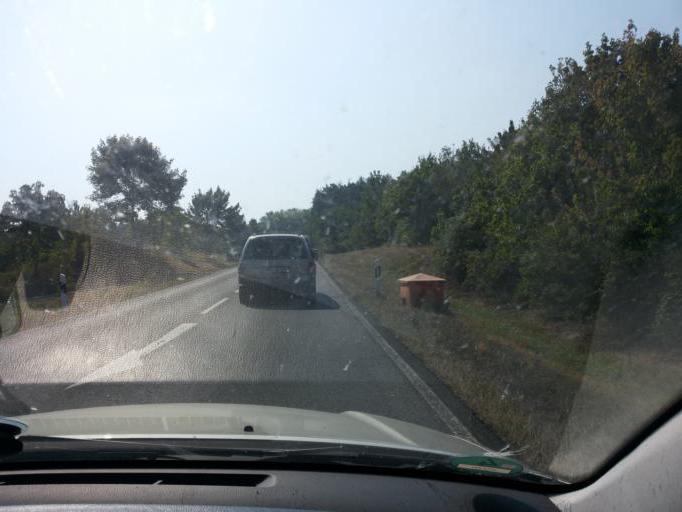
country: DE
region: Bavaria
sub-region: Regierungsbezirk Mittelfranken
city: Ipsheim
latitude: 49.5073
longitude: 10.5013
